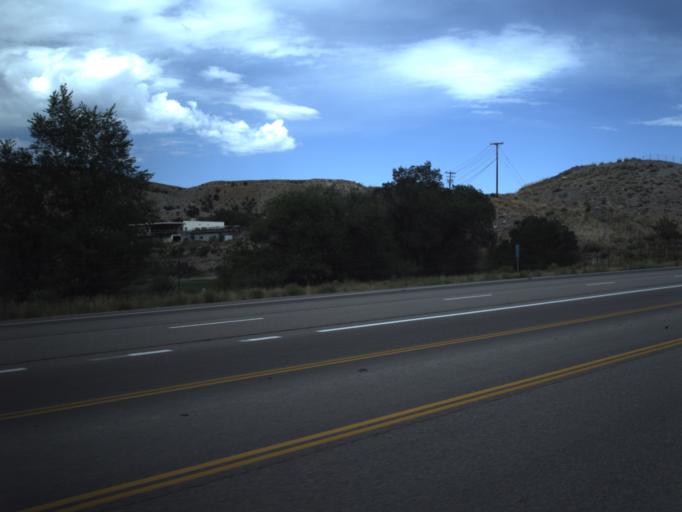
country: US
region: Utah
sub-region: Carbon County
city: Spring Glen
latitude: 39.6439
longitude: -110.8596
